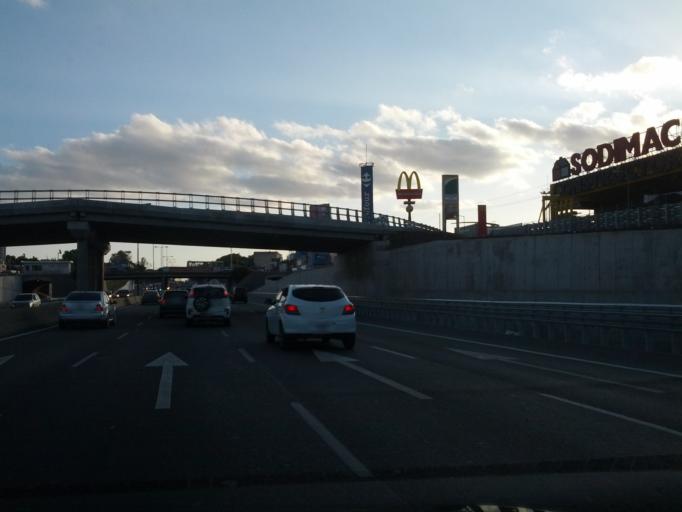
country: AR
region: Buenos Aires
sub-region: Partido de General San Martin
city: General San Martin
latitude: -34.5877
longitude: -58.5179
